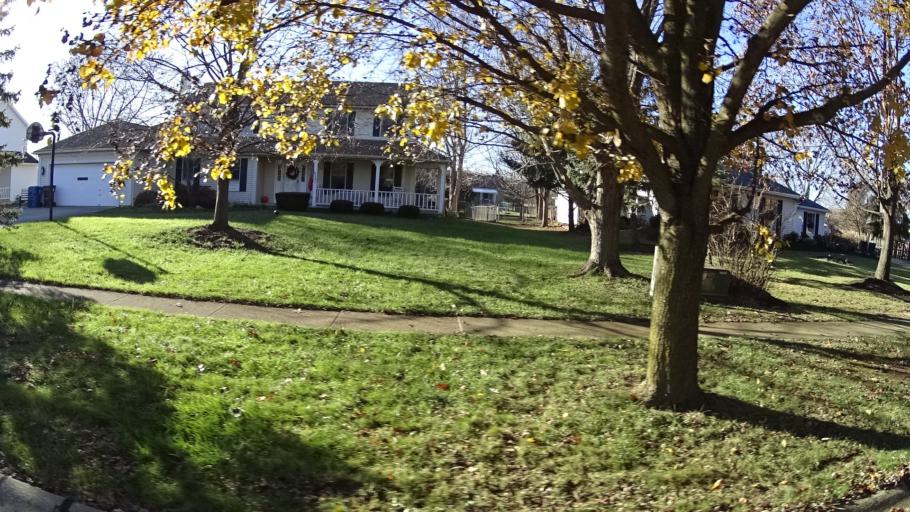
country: US
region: Ohio
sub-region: Lorain County
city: Avon Center
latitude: 41.4381
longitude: -82.0013
